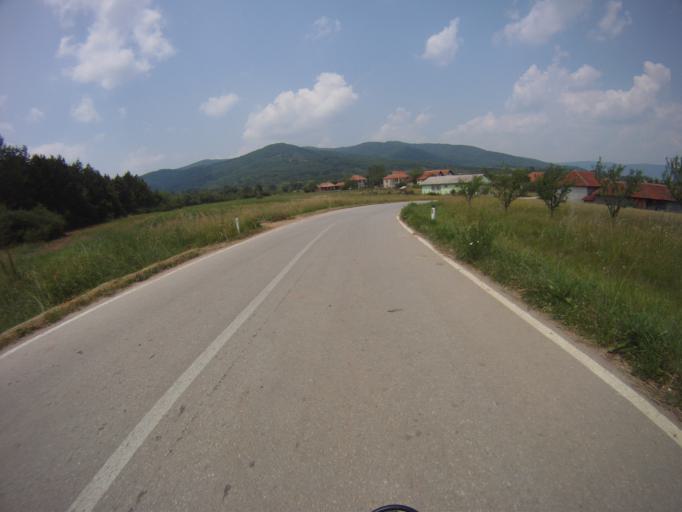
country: RS
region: Central Serbia
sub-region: Nisavski Okrug
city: Gadzin Han
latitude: 43.2061
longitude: 21.9845
